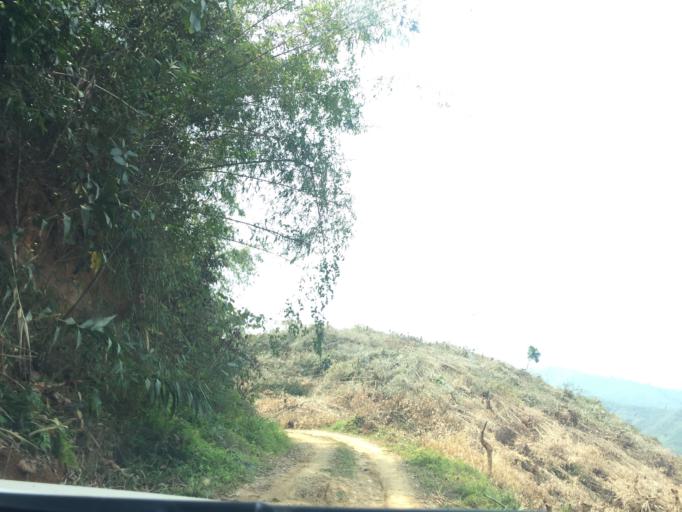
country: LA
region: Loungnamtha
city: Muang Nale
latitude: 20.6076
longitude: 101.6016
